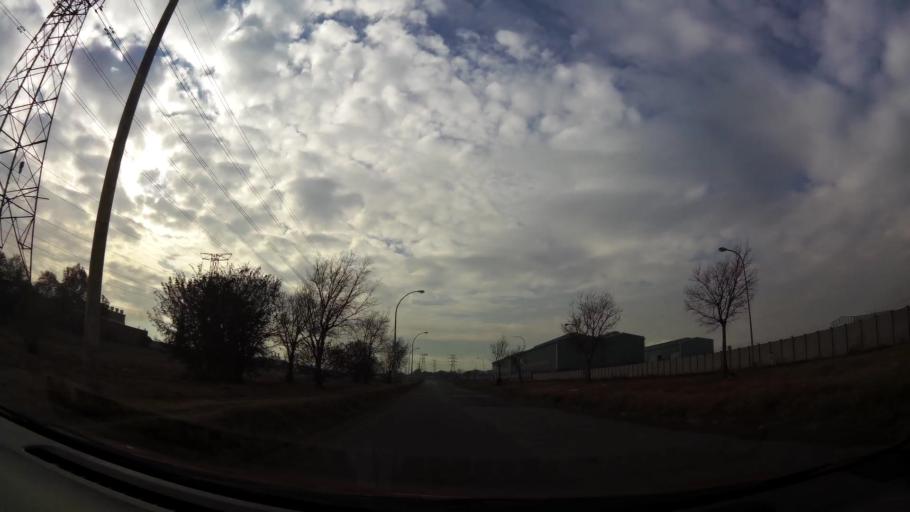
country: ZA
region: Gauteng
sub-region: Sedibeng District Municipality
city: Vanderbijlpark
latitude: -26.6741
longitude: 27.7999
